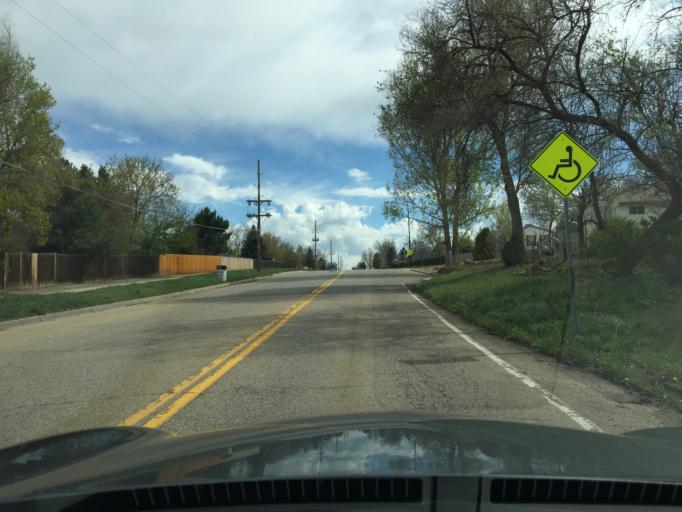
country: US
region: Colorado
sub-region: Boulder County
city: Lafayette
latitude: 40.0107
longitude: -105.0933
